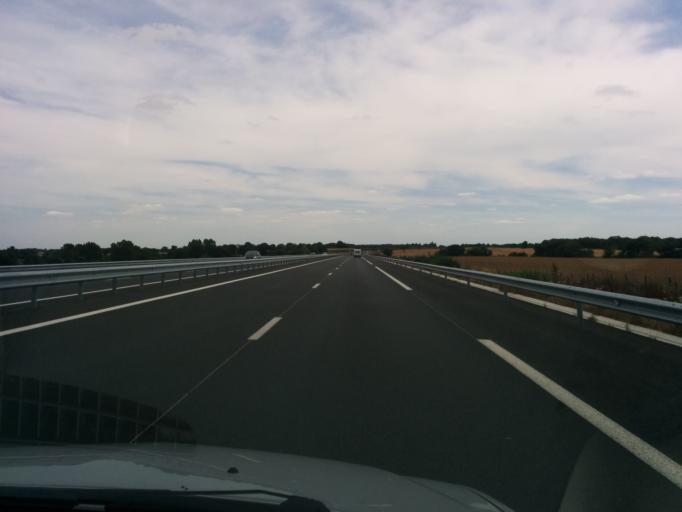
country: FR
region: Poitou-Charentes
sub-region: Departement des Deux-Sevres
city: Nueil-les-Aubiers
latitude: 46.8675
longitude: -0.5750
